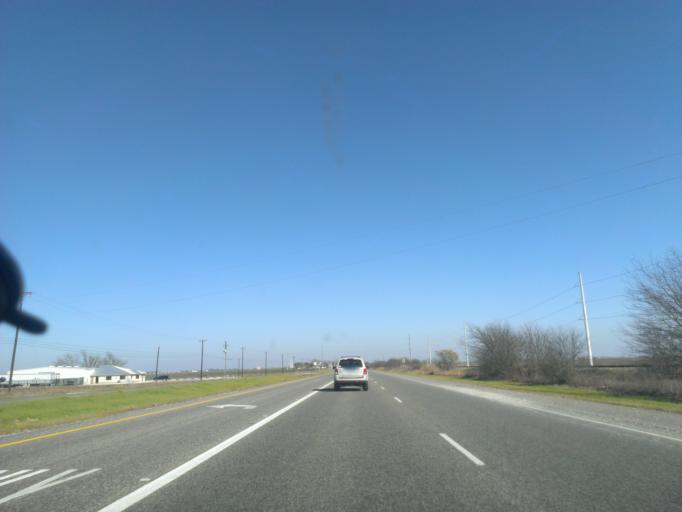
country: US
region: Texas
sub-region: Williamson County
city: Taylor
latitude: 30.5795
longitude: -97.3575
